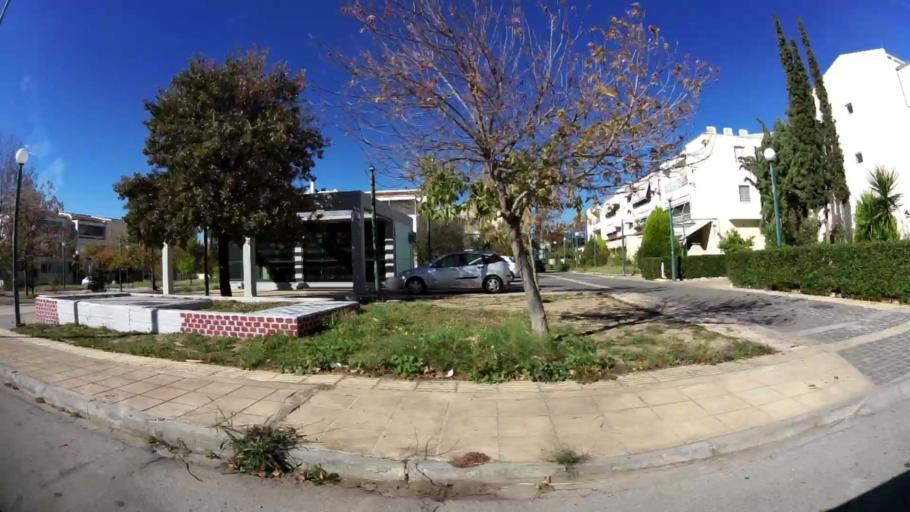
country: GR
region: Attica
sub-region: Nomarchia Anatolikis Attikis
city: Thrakomakedones
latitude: 38.1055
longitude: 23.7671
